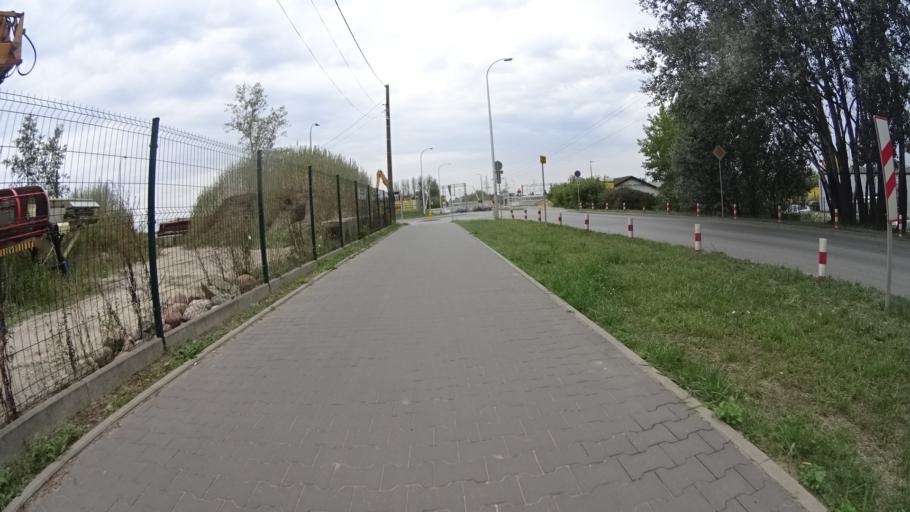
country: PL
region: Masovian Voivodeship
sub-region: Powiat pruszkowski
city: Otrebusy
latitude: 52.1584
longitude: 20.7653
